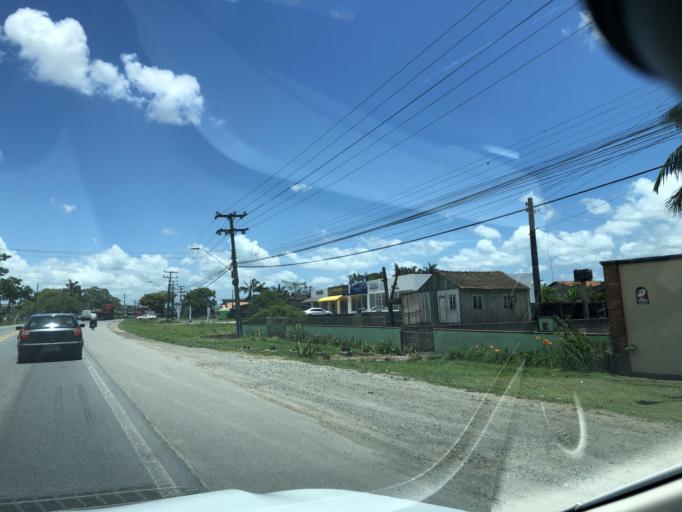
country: BR
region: Santa Catarina
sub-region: Joinville
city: Joinville
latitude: -26.4043
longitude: -48.7454
